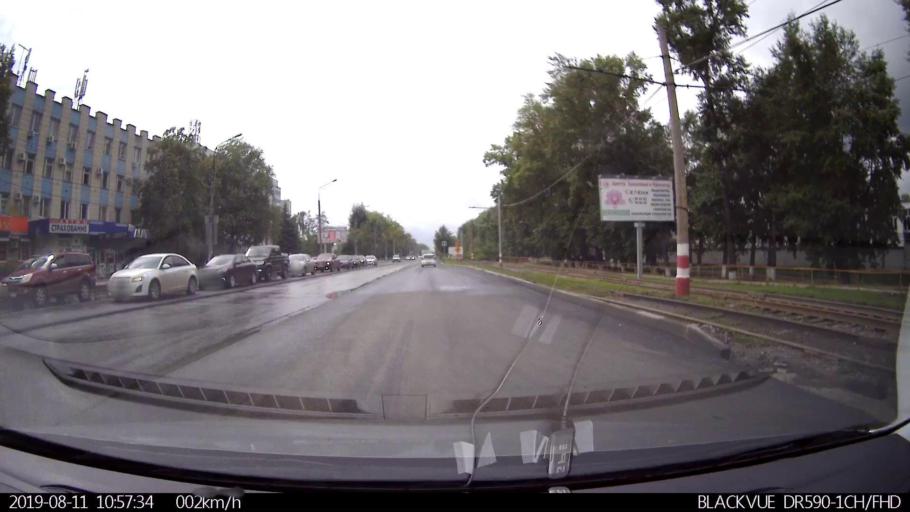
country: RU
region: Ulyanovsk
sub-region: Ulyanovskiy Rayon
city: Ulyanovsk
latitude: 54.2577
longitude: 48.3212
